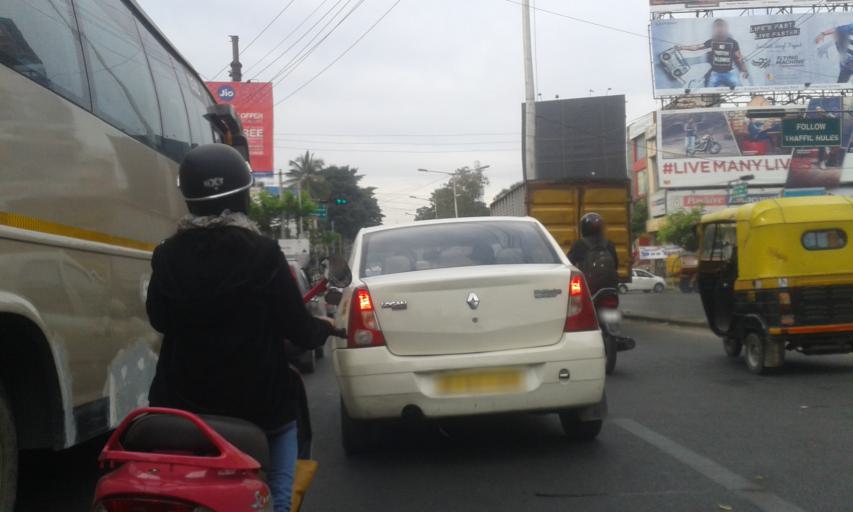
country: IN
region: Karnataka
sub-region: Bangalore Urban
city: Bangalore
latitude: 12.9375
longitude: 77.6273
